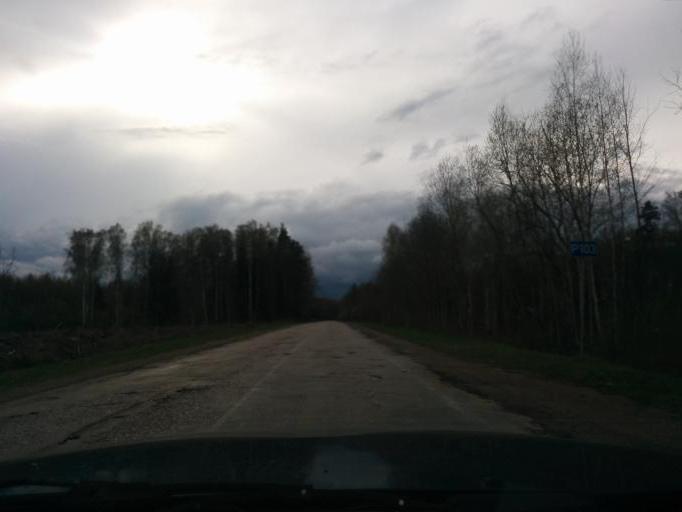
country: LT
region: Siauliu apskritis
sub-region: Joniskis
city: Joniskis
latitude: 56.4164
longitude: 23.6129
